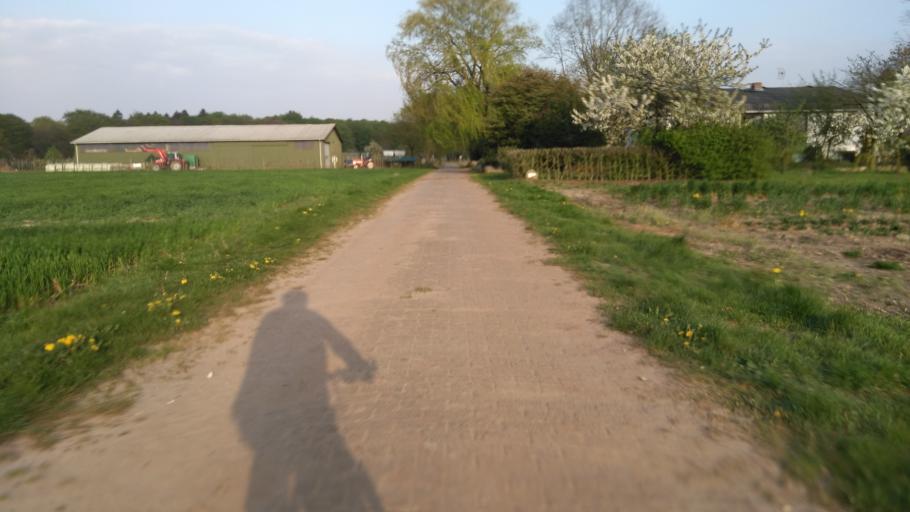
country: DE
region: Lower Saxony
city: Nottensdorf
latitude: 53.4684
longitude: 9.6285
